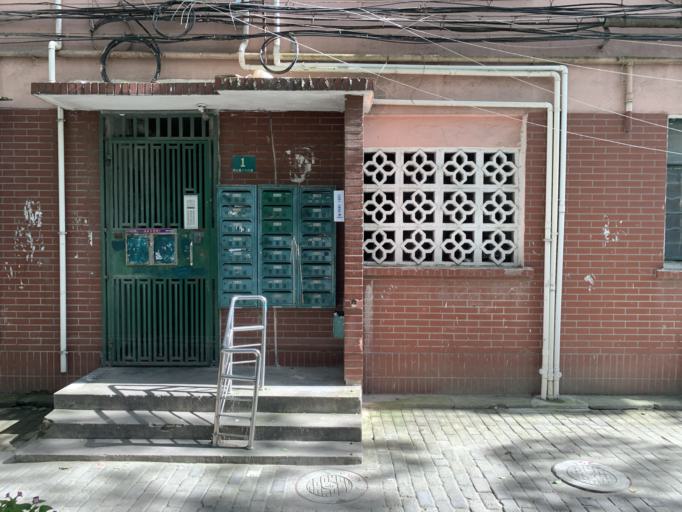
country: CN
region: Shanghai Shi
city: Pudong
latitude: 31.2165
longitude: 121.5222
